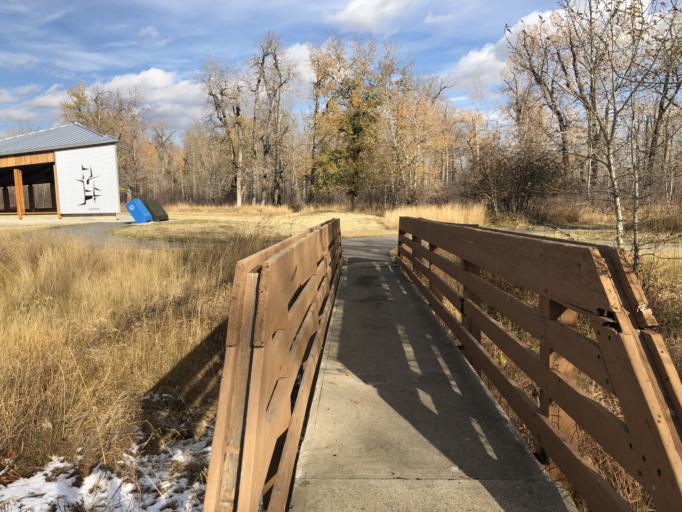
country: CA
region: Alberta
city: Calgary
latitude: 50.9268
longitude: -114.0631
